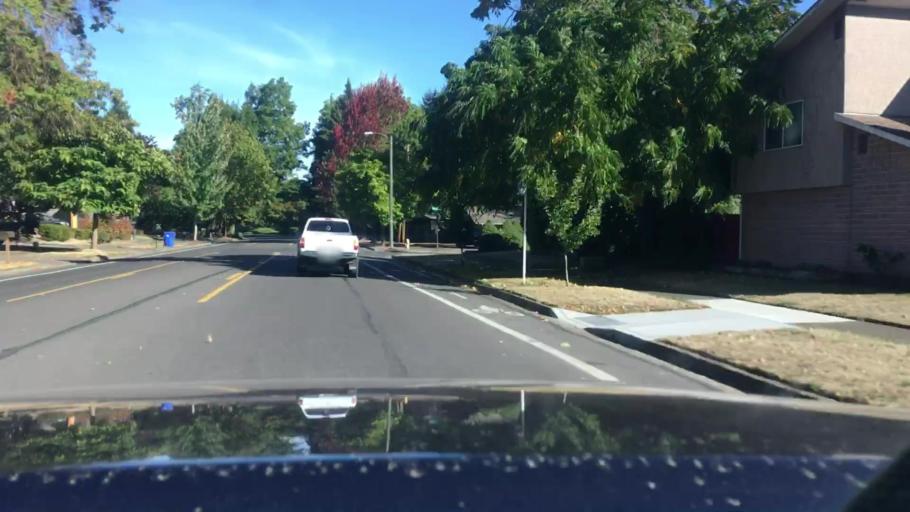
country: US
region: Oregon
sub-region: Lane County
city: Eugene
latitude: 44.0695
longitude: -123.0677
